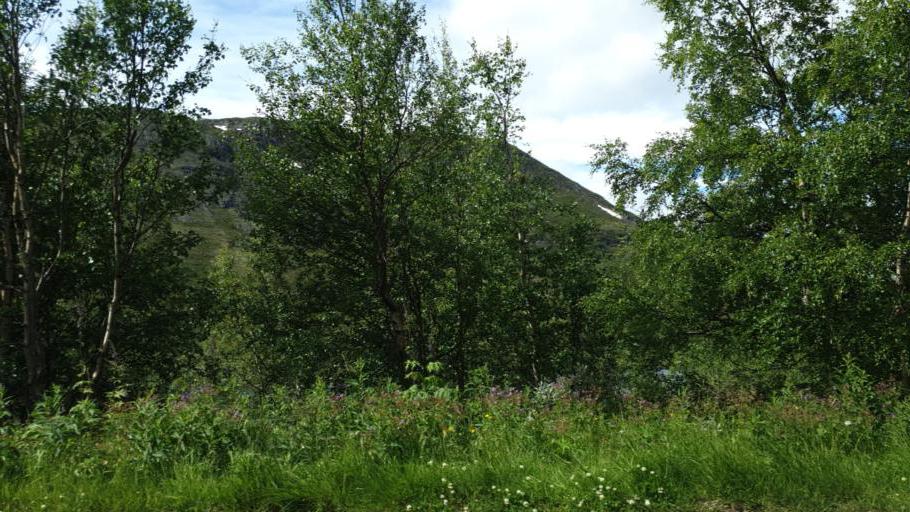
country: NO
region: Oppland
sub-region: Lom
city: Fossbergom
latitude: 61.4922
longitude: 8.8164
